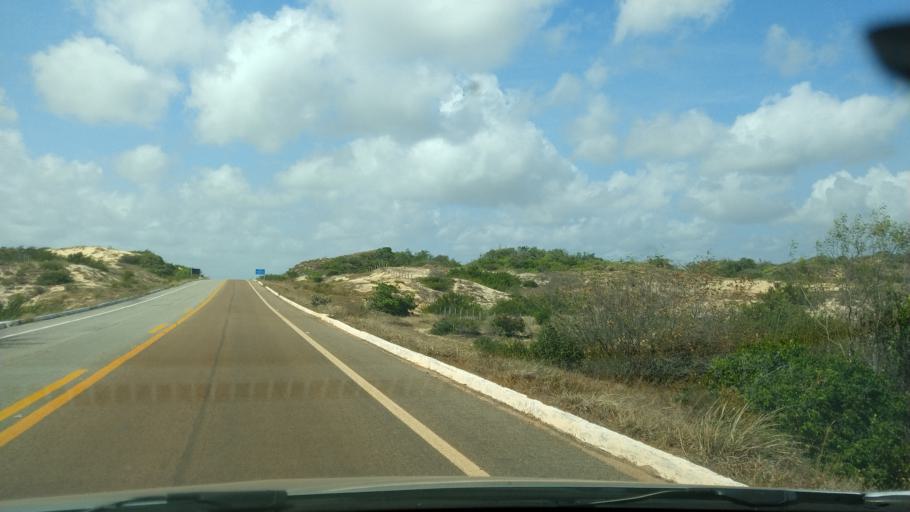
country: BR
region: Rio Grande do Norte
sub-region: Touros
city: Touros
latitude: -5.1614
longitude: -35.5019
